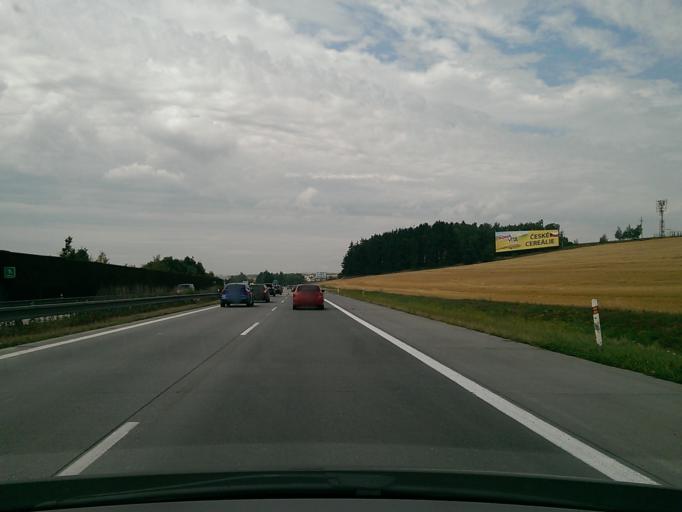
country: CZ
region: Vysocina
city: Merin
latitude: 49.3952
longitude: 15.8907
